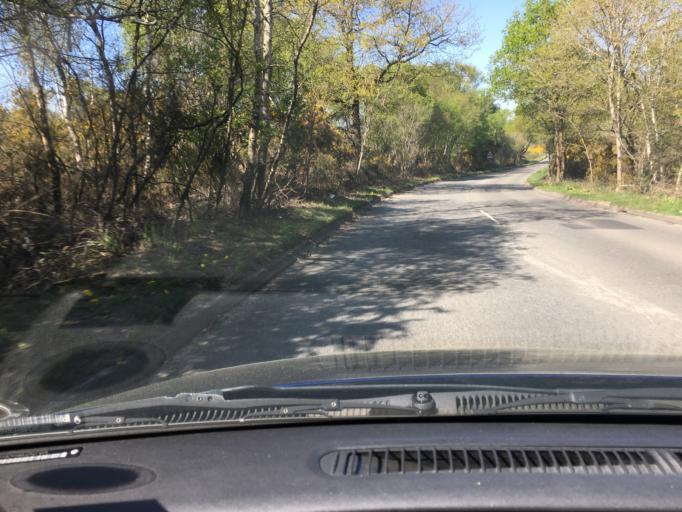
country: GB
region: England
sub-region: Hampshire
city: Yateley
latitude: 51.3259
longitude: -0.8249
